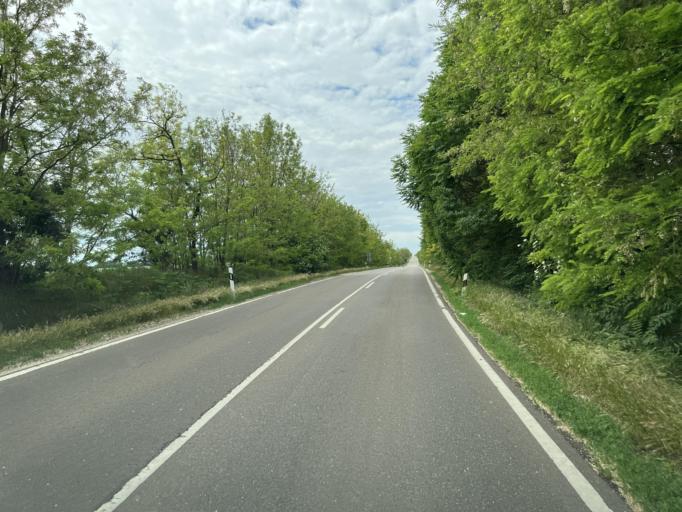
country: HU
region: Pest
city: Zsambok
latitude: 47.5351
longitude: 19.6047
